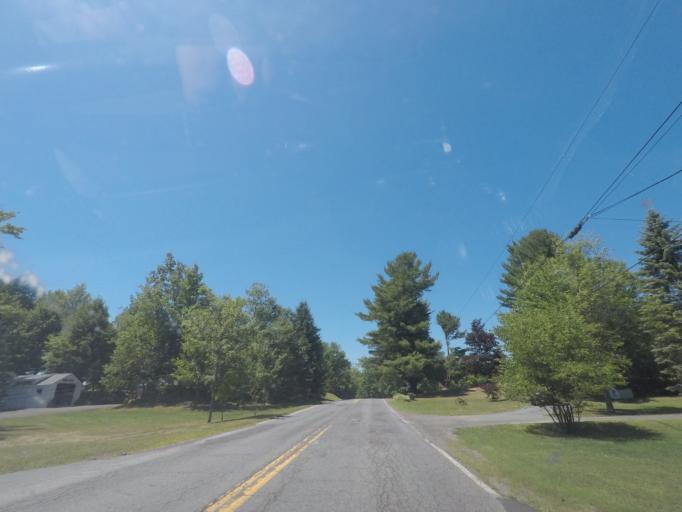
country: US
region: New York
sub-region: Rensselaer County
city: West Sand Lake
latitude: 42.6214
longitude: -73.5882
